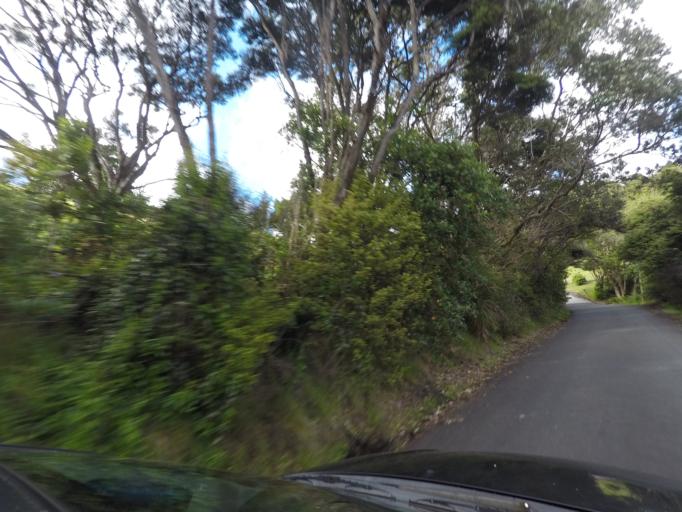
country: NZ
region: Auckland
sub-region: Auckland
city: Titirangi
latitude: -37.0197
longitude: 174.5505
